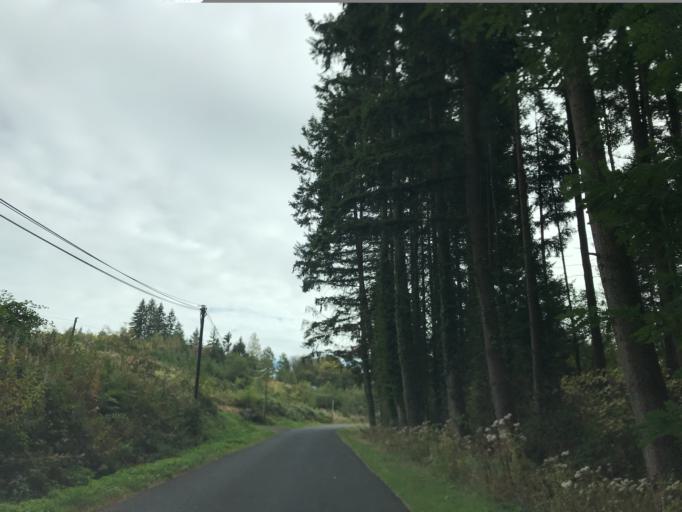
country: FR
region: Auvergne
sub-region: Departement du Puy-de-Dome
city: Escoutoux
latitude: 45.8297
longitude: 3.5791
